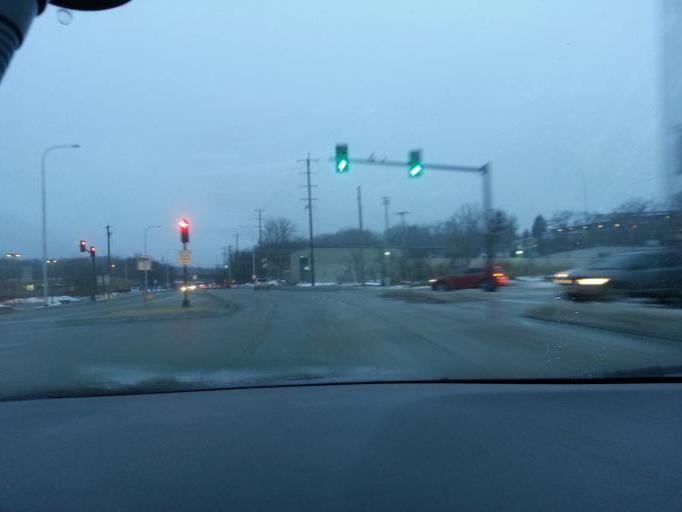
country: US
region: Illinois
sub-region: McHenry County
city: Algonquin
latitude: 42.1700
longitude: -88.2966
